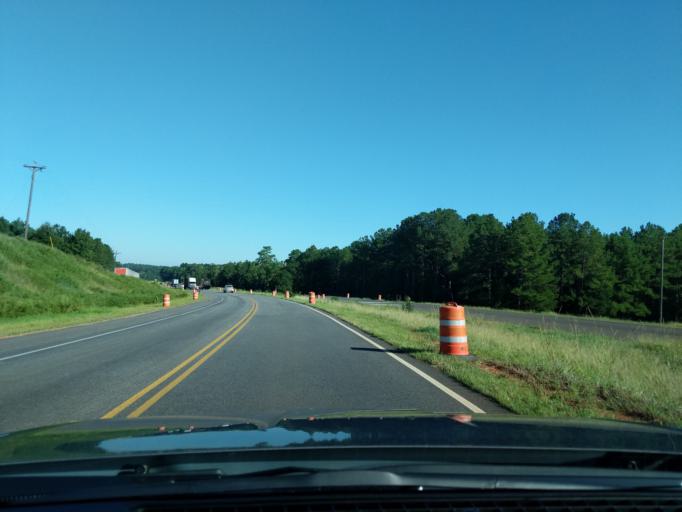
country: US
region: Georgia
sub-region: McDuffie County
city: Thomson
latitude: 33.5732
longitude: -82.5204
